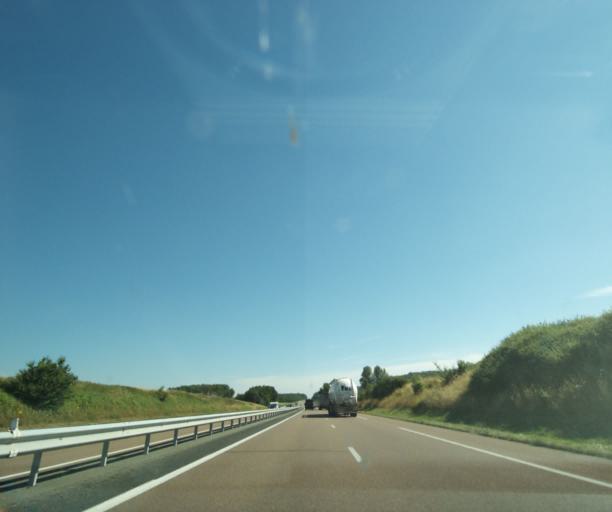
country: FR
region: Champagne-Ardenne
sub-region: Departement de la Haute-Marne
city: Saulxures
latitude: 48.0515
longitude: 5.5773
